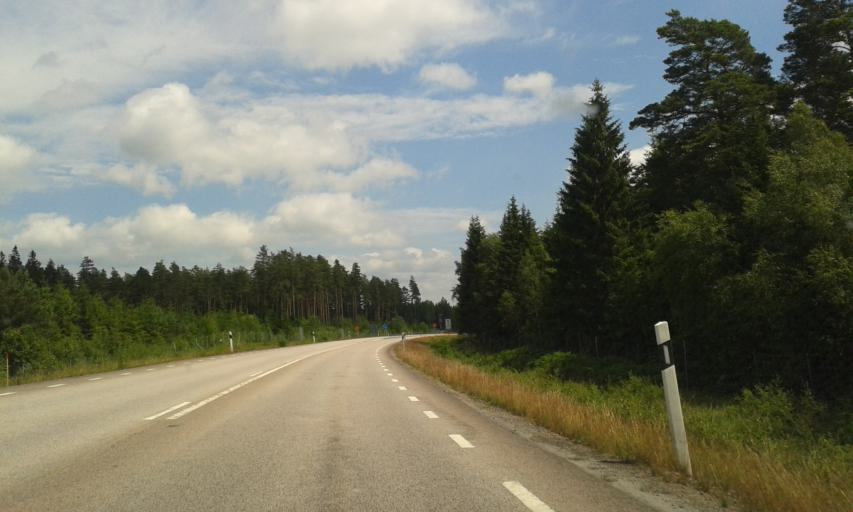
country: SE
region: Kronoberg
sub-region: Alvesta Kommun
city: Alvesta
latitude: 56.9140
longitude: 14.4852
